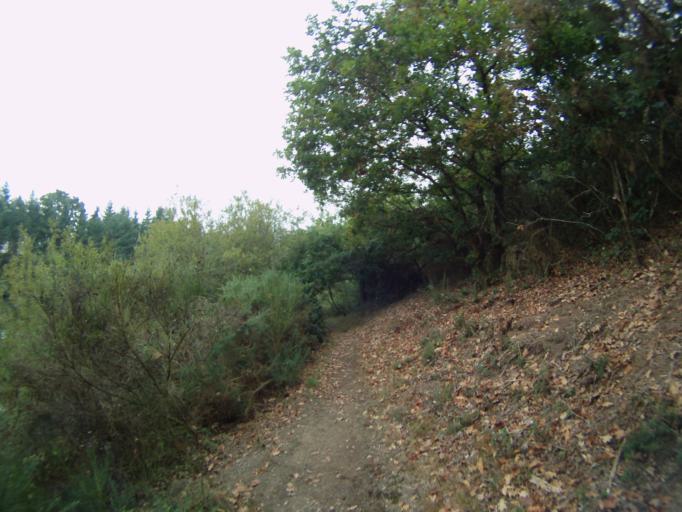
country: FR
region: Brittany
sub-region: Departement d'Ille-et-Vilaine
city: Chanteloup
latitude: 47.9721
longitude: -1.6040
